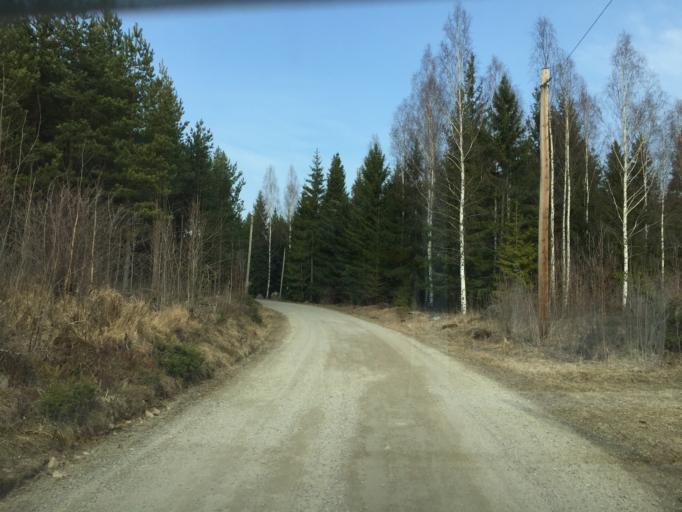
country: SE
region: Soedermanland
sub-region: Vingakers Kommun
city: Vingaker
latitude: 59.0197
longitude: 15.7782
